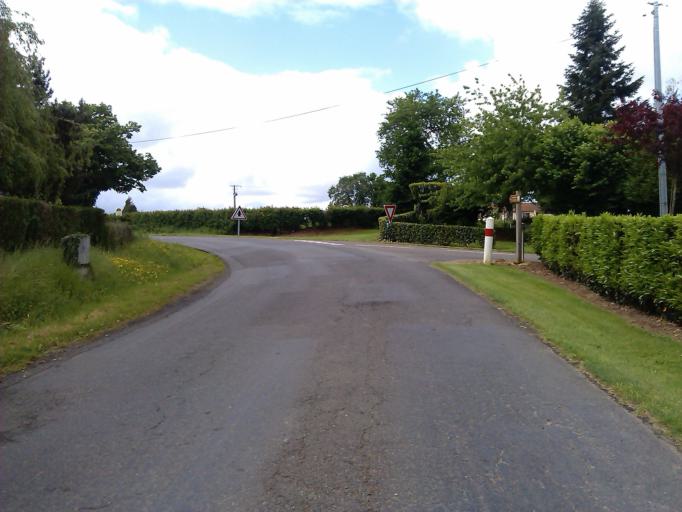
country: FR
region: Poitou-Charentes
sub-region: Departement de la Vienne
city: Availles-Limouzine
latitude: 46.1371
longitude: 0.5911
